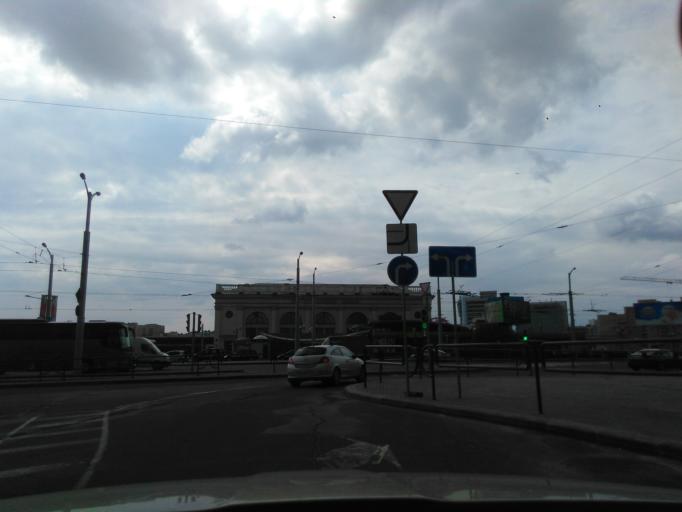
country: BY
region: Minsk
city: Minsk
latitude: 53.8923
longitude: 27.5488
